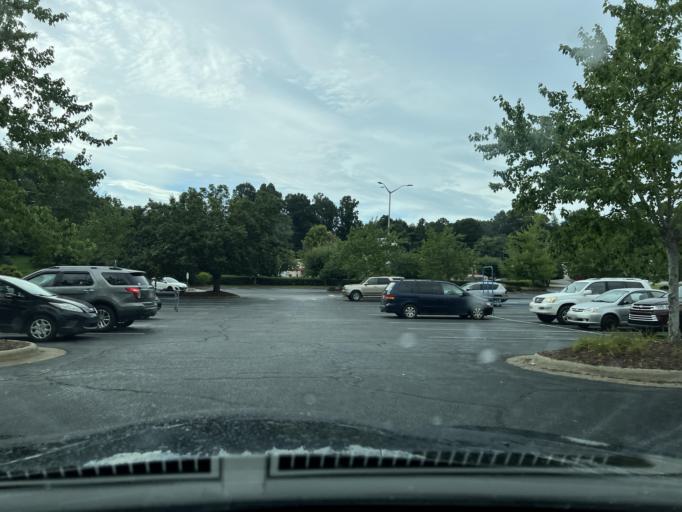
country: US
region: North Carolina
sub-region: Buncombe County
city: Bent Creek
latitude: 35.5711
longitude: -82.6178
